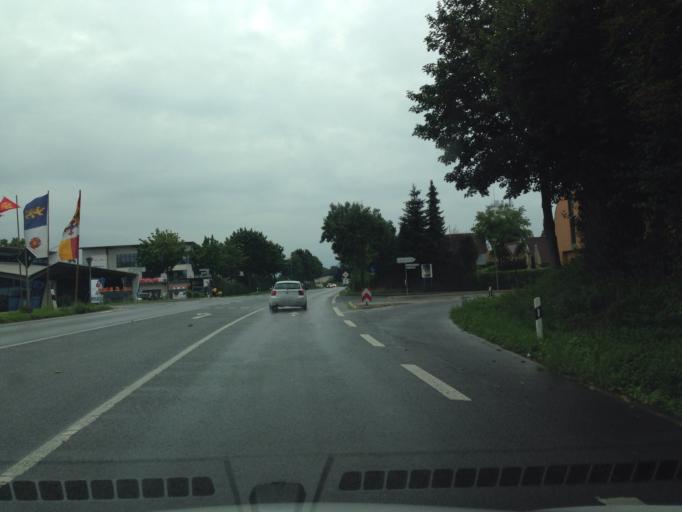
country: DE
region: North Rhine-Westphalia
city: Erkelenz
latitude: 51.0741
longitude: 6.3304
